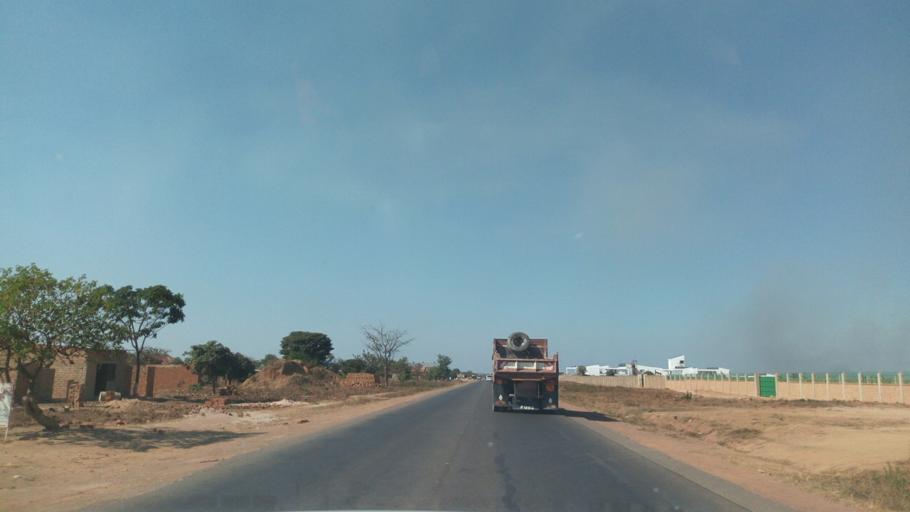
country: CD
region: Katanga
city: Lubumbashi
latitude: -11.5783
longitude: 27.5286
